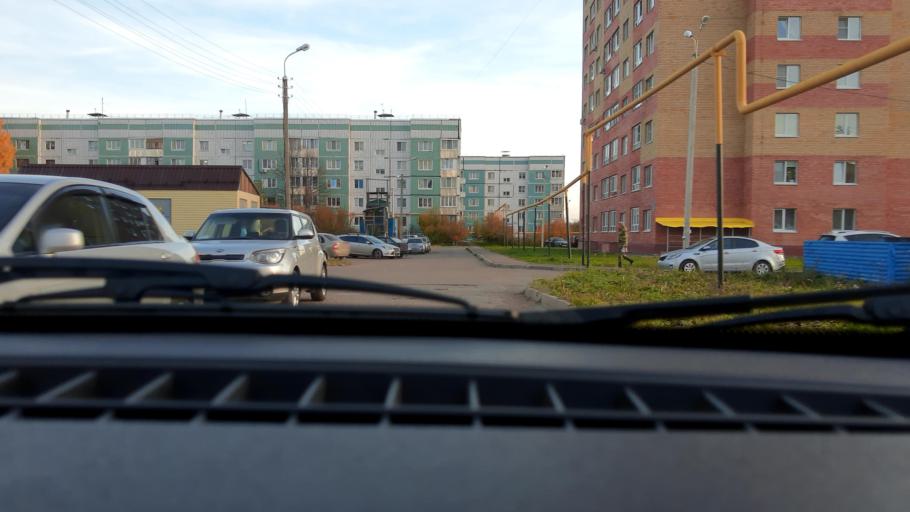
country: RU
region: Bashkortostan
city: Mikhaylovka
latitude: 54.7926
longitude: 55.8618
